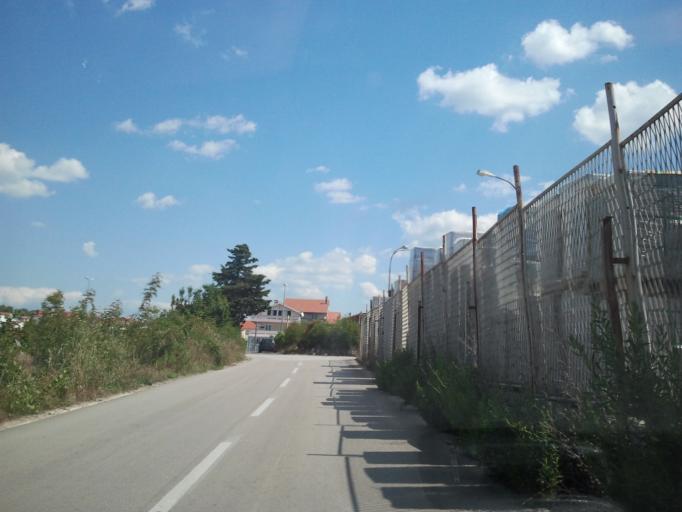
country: HR
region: Zadarska
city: Zadar
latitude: 44.1068
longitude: 15.2598
